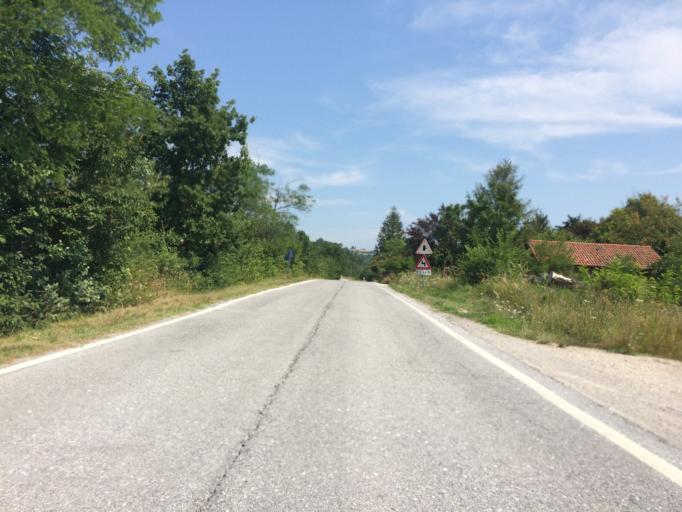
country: IT
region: Piedmont
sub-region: Provincia di Cuneo
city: Cissone
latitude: 44.5612
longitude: 8.0367
